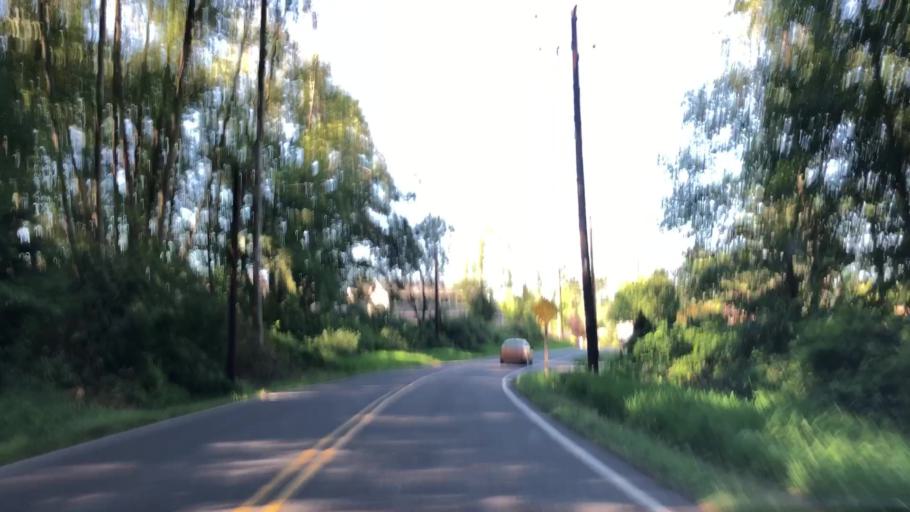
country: US
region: Washington
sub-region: Snohomish County
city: Martha Lake
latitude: 47.8584
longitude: -122.2708
